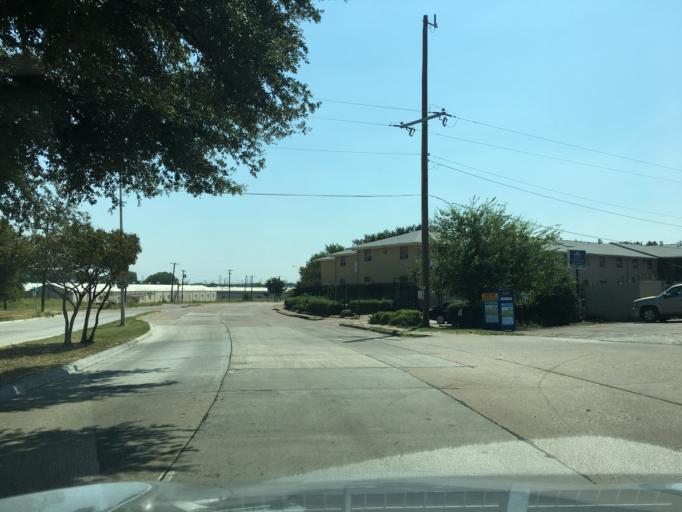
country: US
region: Texas
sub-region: Dallas County
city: Dallas
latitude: 32.7392
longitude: -96.7891
